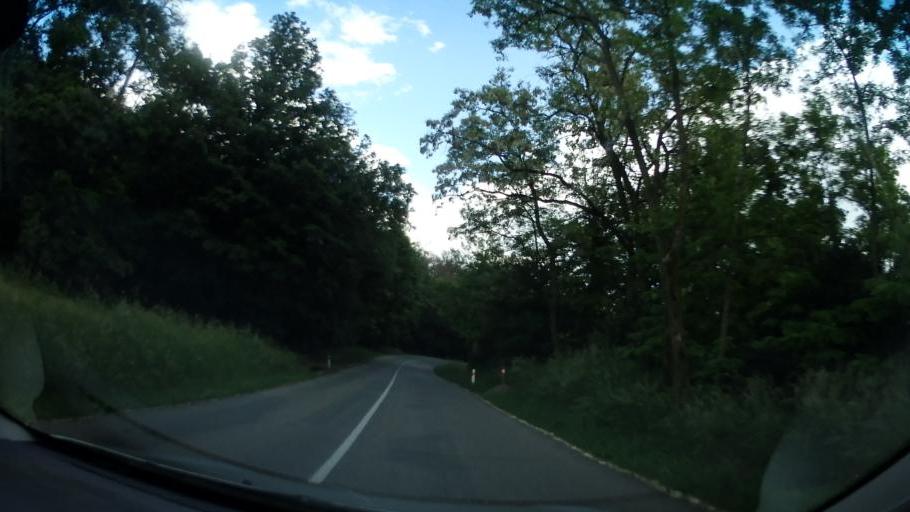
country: CZ
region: South Moravian
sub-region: Okres Brno-Venkov
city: Dolni Loucky
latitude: 49.3665
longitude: 16.3752
